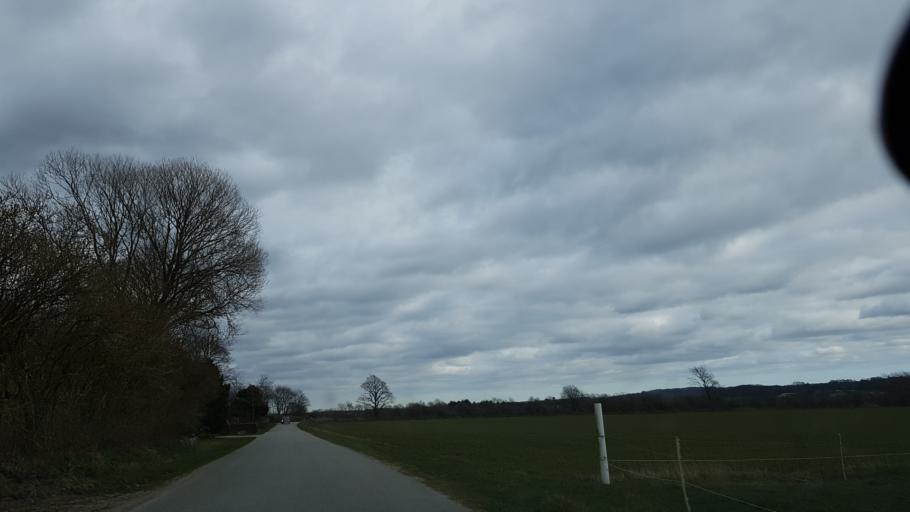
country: DK
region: South Denmark
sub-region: Vejen Kommune
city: Brorup
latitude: 55.4472
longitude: 8.9820
